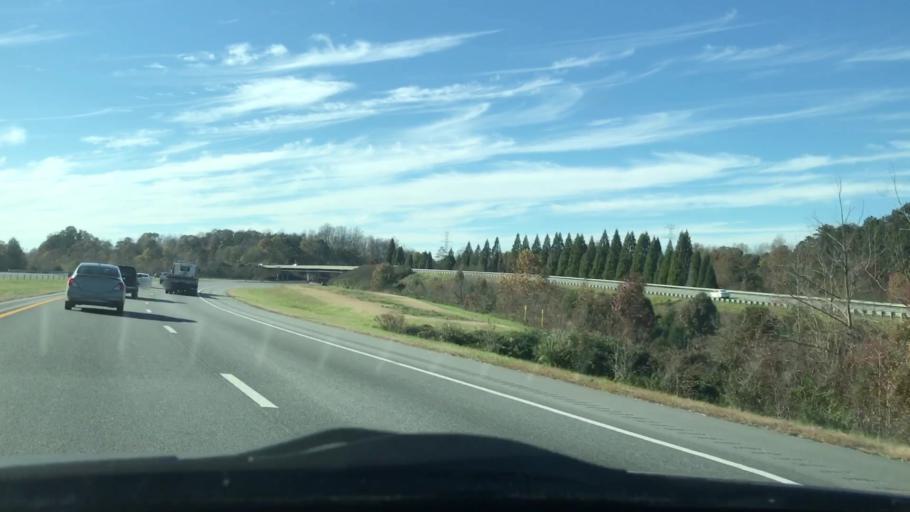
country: US
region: North Carolina
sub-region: Guilford County
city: High Point
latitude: 36.0076
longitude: -80.0269
